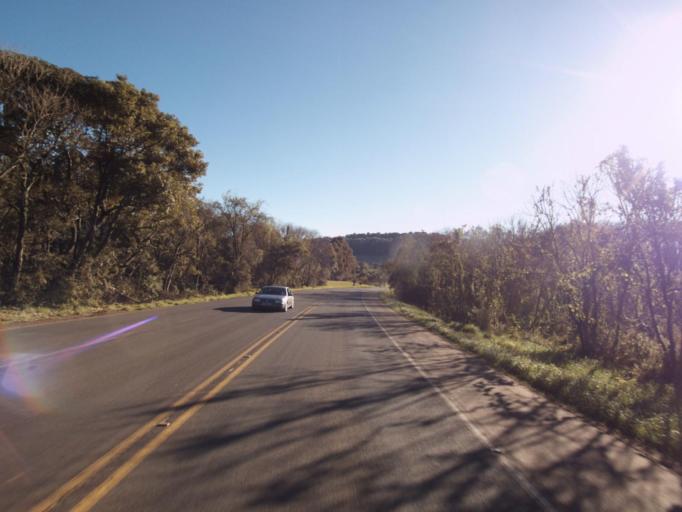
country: BR
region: Santa Catarina
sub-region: Chapeco
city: Chapeco
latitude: -26.9979
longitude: -52.6961
